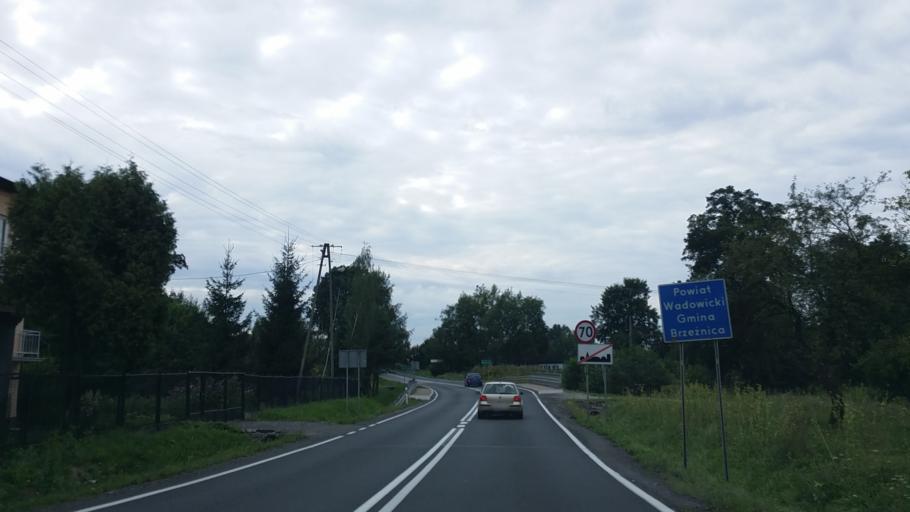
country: PL
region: Lesser Poland Voivodeship
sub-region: Powiat krakowski
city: Czernichow
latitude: 49.9604
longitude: 19.6598
